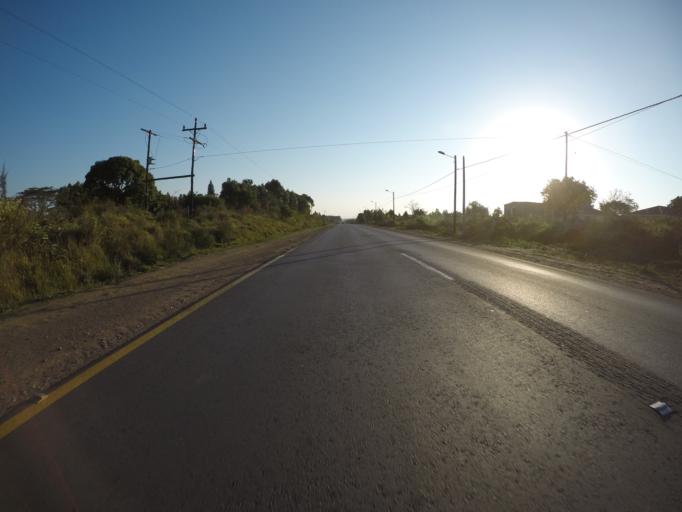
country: ZA
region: KwaZulu-Natal
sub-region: uThungulu District Municipality
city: KwaMbonambi
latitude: -28.6830
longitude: 32.2011
